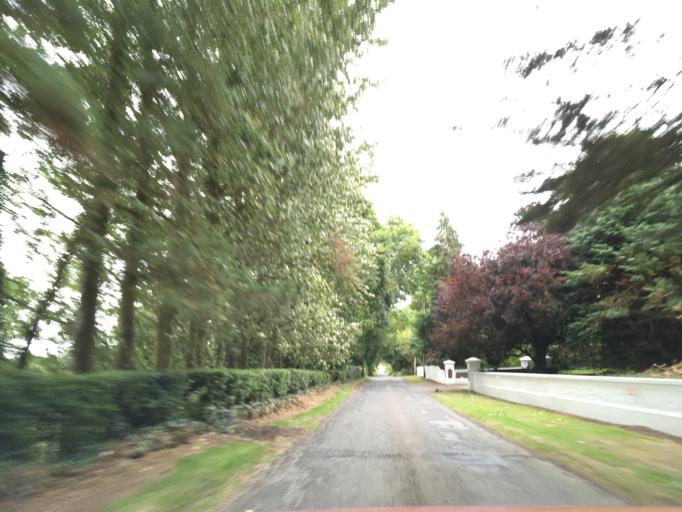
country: IE
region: Munster
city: Cashel
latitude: 52.4725
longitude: -7.9123
